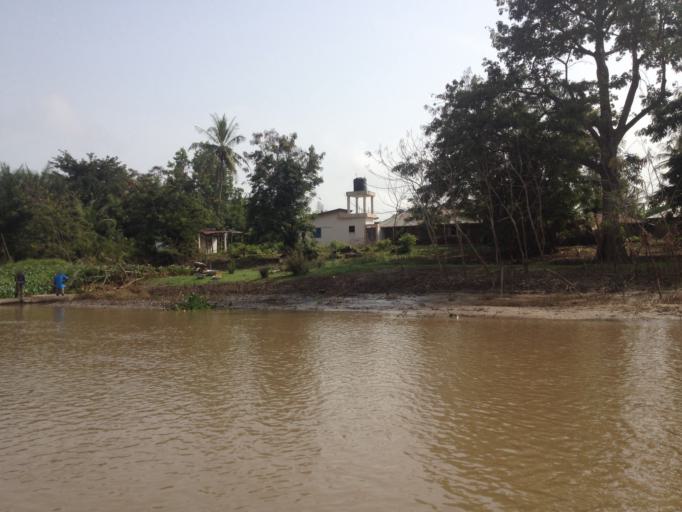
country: BJ
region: Mono
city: Grand-Popo
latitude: 6.3726
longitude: 1.7826
